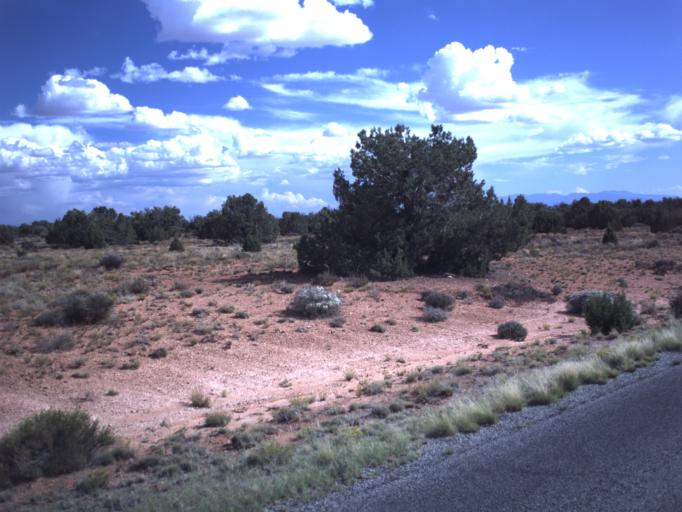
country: US
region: Utah
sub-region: Grand County
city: Moab
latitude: 38.4818
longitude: -109.7389
